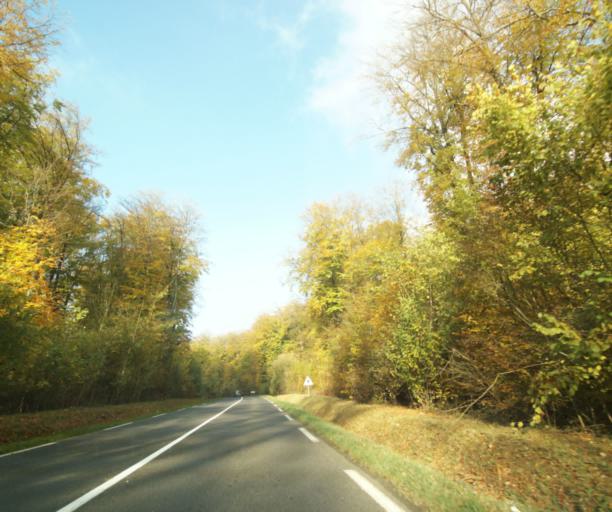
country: FR
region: Lorraine
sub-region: Departement de Meurthe-et-Moselle
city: Briey
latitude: 49.2624
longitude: 5.9305
